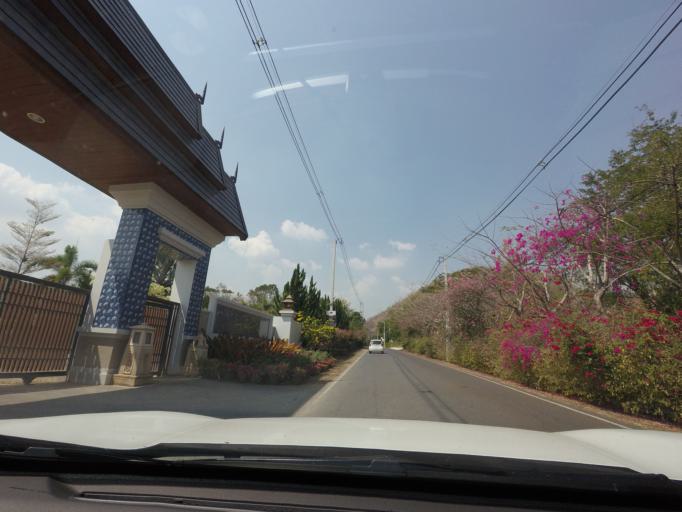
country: TH
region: Nakhon Ratchasima
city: Pak Chong
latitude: 14.5783
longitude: 101.4351
